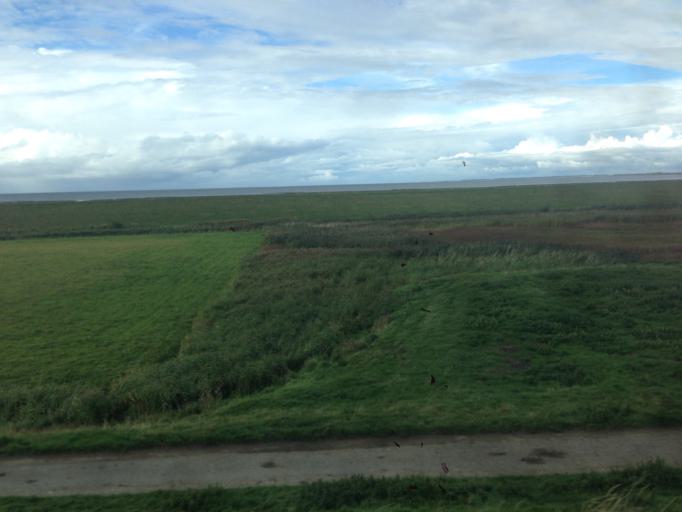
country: DE
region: Schleswig-Holstein
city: Friedrich-Wilhelm-Lubke-Koog
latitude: 54.8867
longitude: 8.6138
